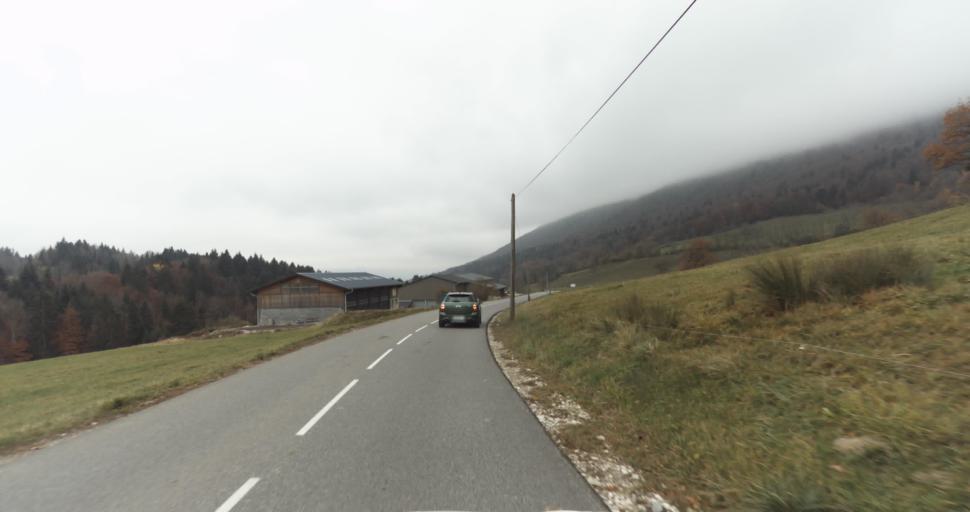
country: FR
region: Rhone-Alpes
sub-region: Departement de la Haute-Savoie
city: Gruffy
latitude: 45.7651
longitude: 6.1253
